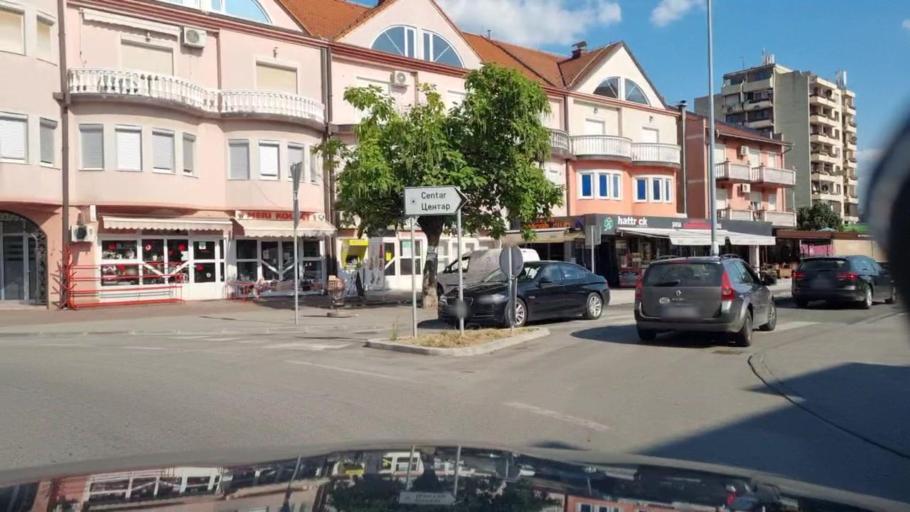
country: BA
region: Federation of Bosnia and Herzegovina
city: Odzak
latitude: 45.0138
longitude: 18.3258
